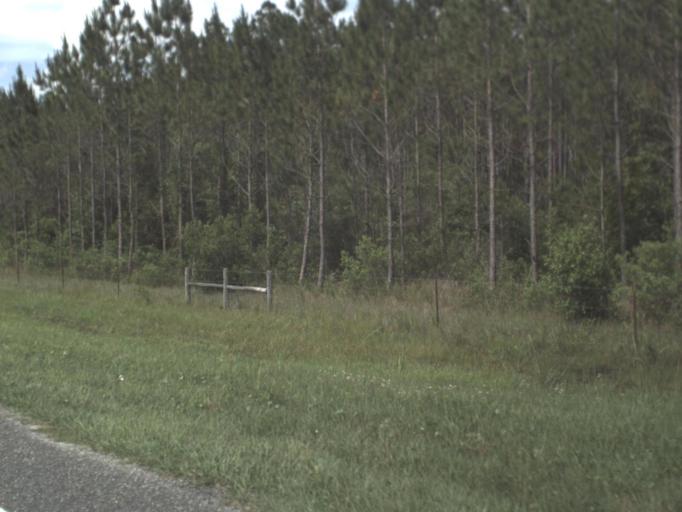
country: US
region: Florida
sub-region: Clay County
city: Middleburg
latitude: 29.9901
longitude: -81.8977
